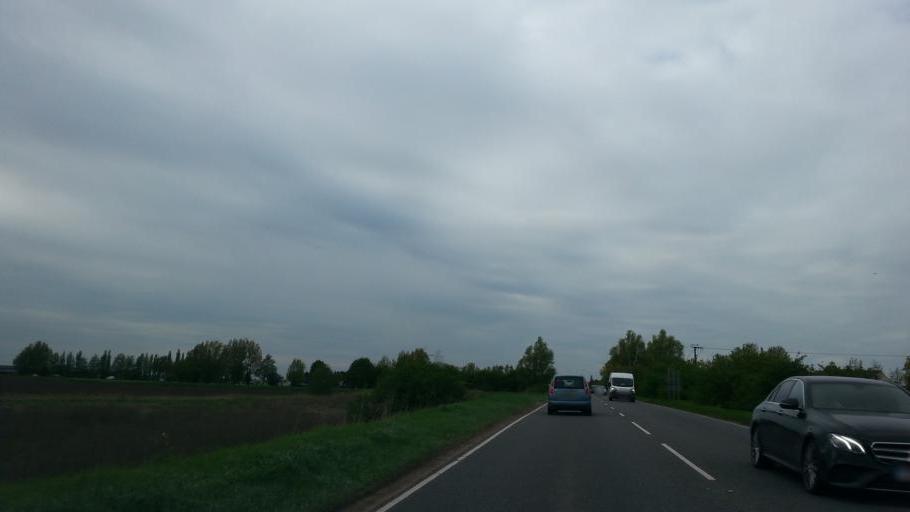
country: GB
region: England
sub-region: Cambridgeshire
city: March
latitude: 52.5514
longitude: 0.0686
